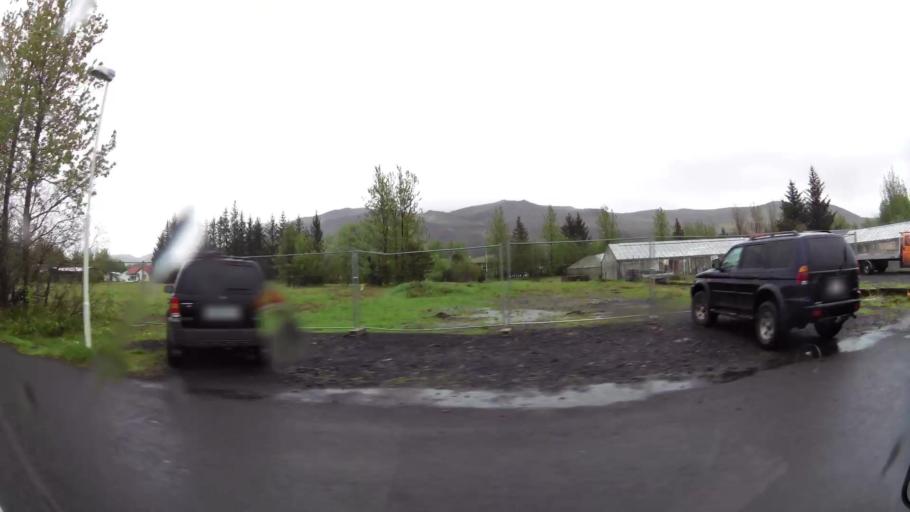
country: IS
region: South
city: Hveragerdi
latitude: 63.9964
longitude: -21.1813
